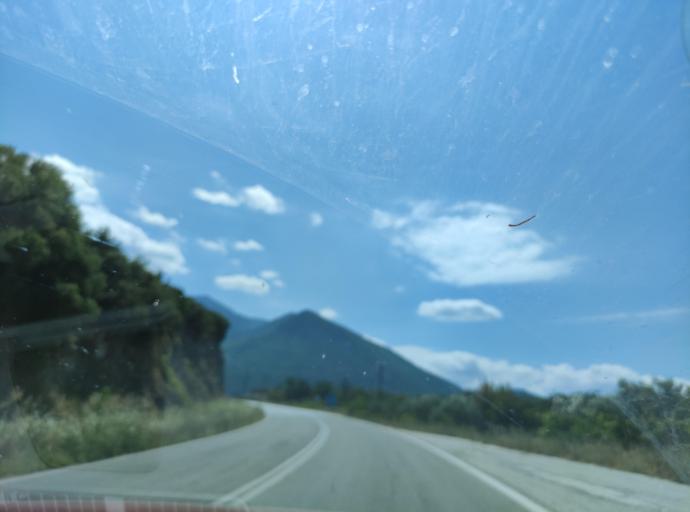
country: GR
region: East Macedonia and Thrace
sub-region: Nomos Kavalas
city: Nikisiani
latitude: 40.9727
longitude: 24.1597
